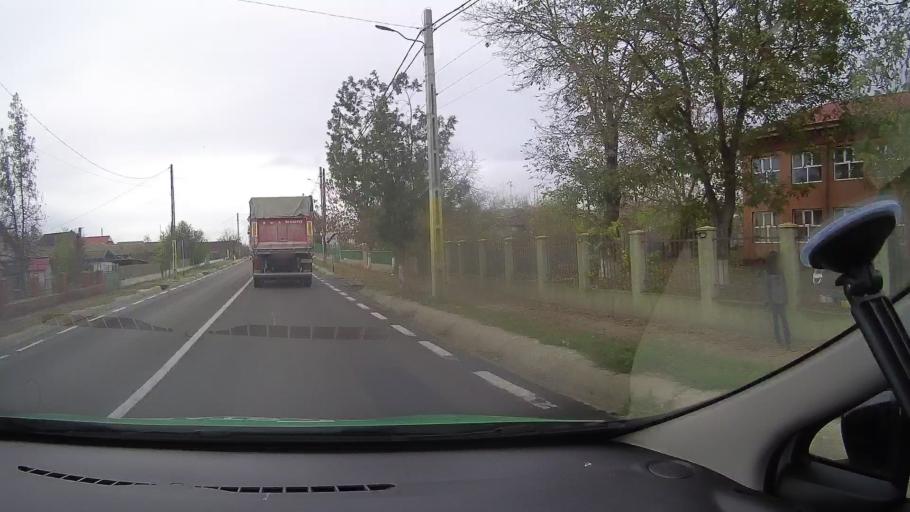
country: RO
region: Constanta
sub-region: Comuna Poarta Alba
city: Poarta Alba
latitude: 44.2092
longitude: 28.3947
